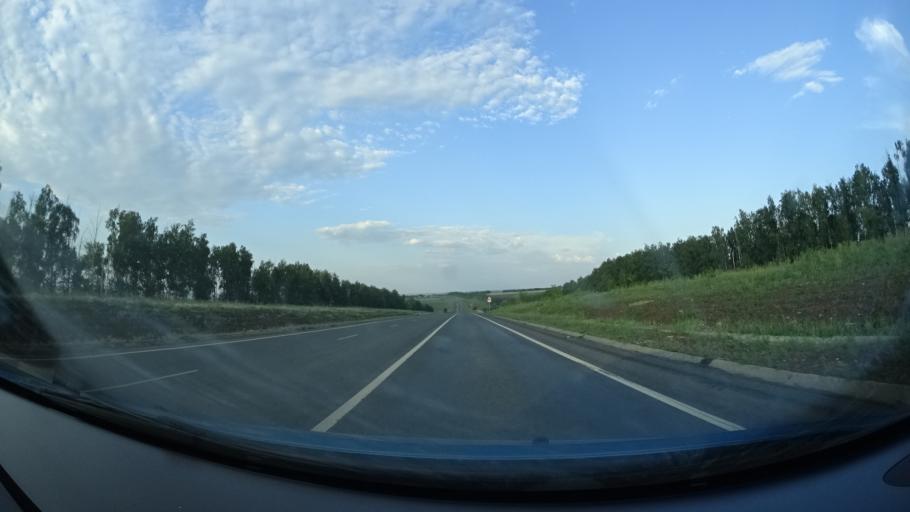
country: RU
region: Samara
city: Klyavlino
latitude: 54.0244
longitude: 51.8645
